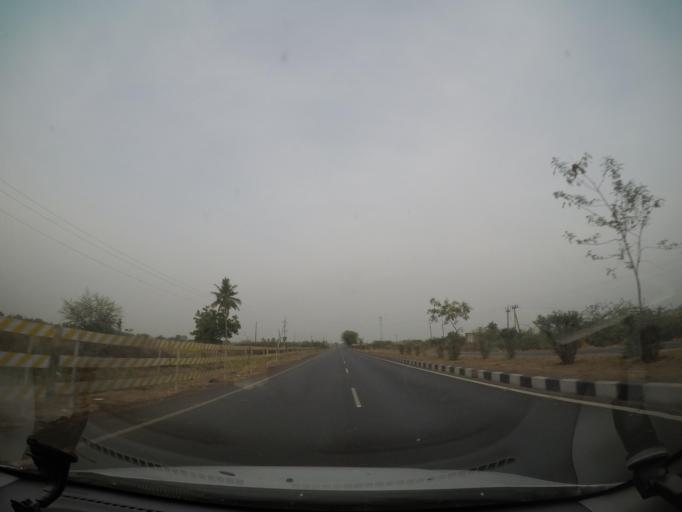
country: IN
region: Andhra Pradesh
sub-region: Krishna
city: Gannavaram
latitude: 16.6296
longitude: 80.9463
